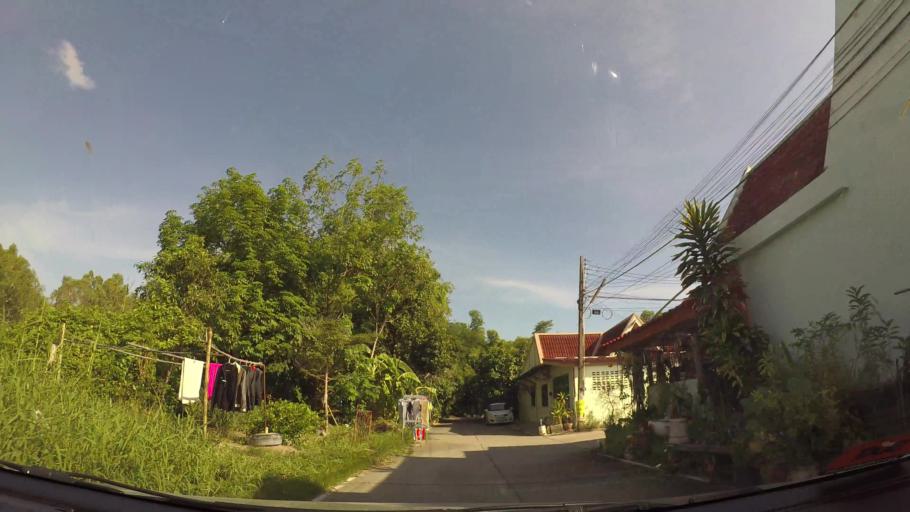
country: TH
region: Rayong
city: Rayong
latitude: 12.6705
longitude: 101.3020
